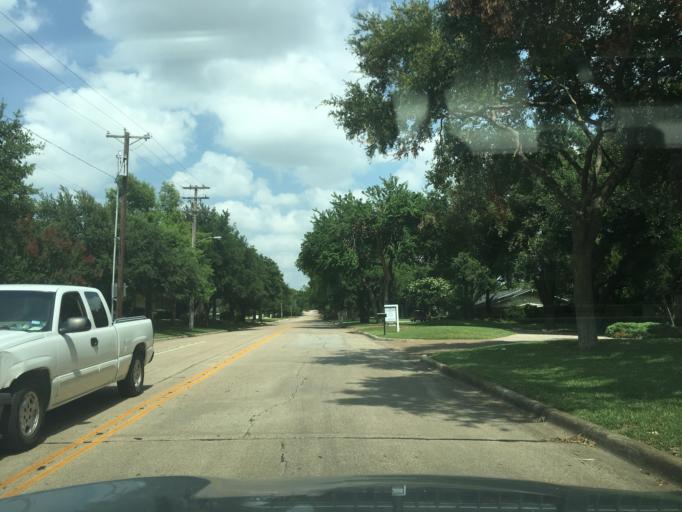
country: US
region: Texas
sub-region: Dallas County
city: University Park
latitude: 32.9023
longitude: -96.8185
